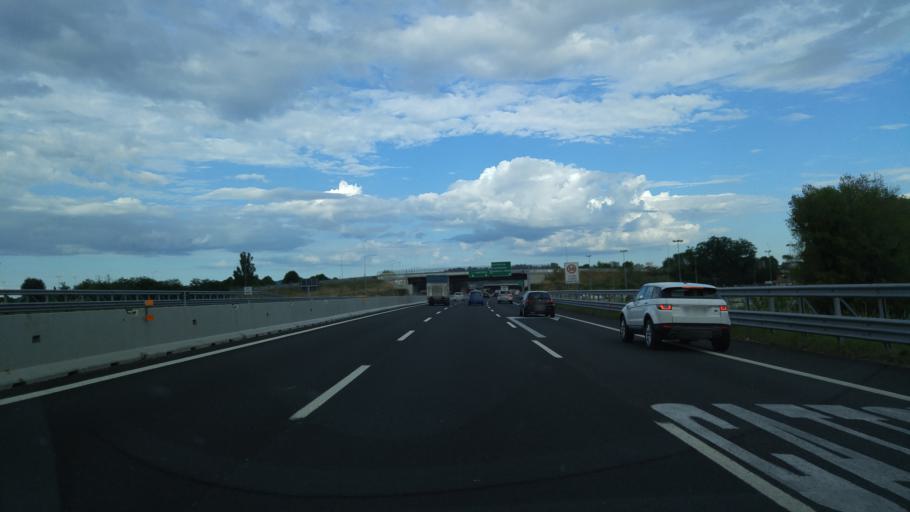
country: IT
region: Emilia-Romagna
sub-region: Provincia di Rimini
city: Montalbano
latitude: 43.9530
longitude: 12.7217
